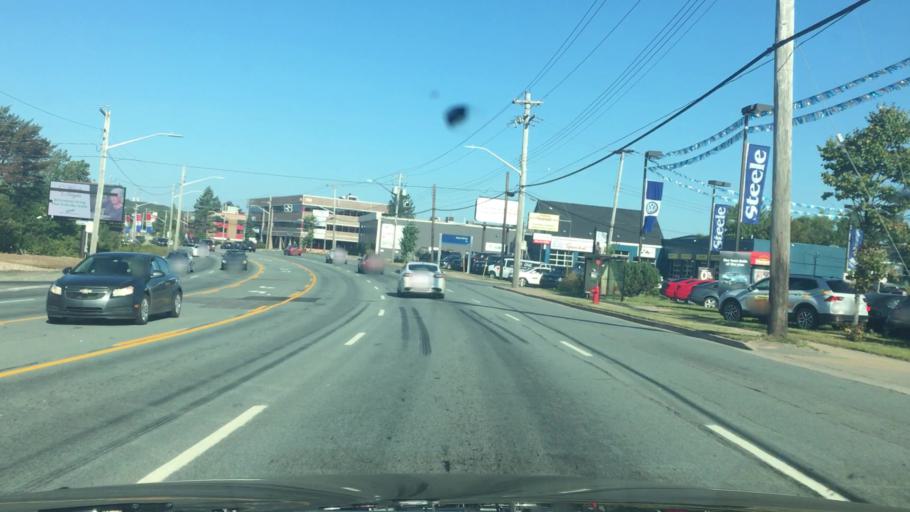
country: CA
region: Nova Scotia
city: Dartmouth
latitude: 44.7019
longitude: -63.6079
